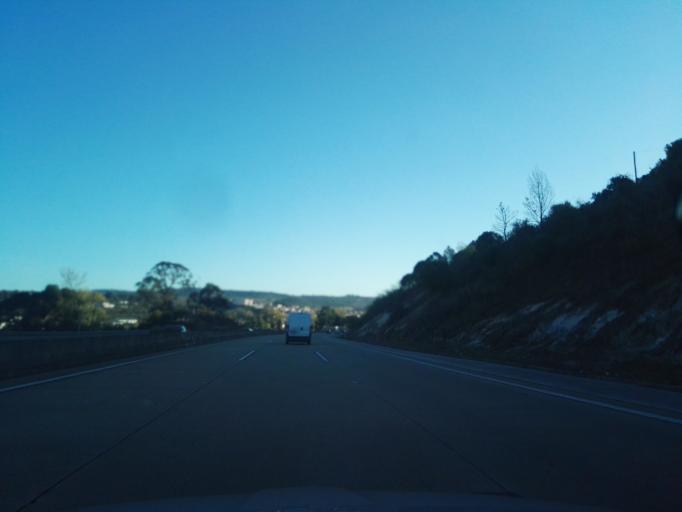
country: PT
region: Lisbon
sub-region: Loures
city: Bucelas
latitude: 38.8970
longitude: -9.1146
